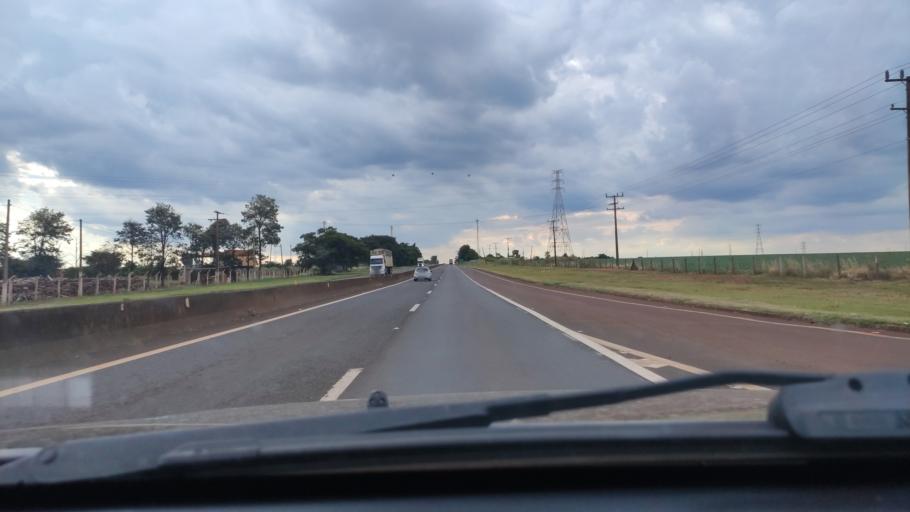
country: BR
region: Sao Paulo
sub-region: Palmital
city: Palmital
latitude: -22.8129
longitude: -50.0593
